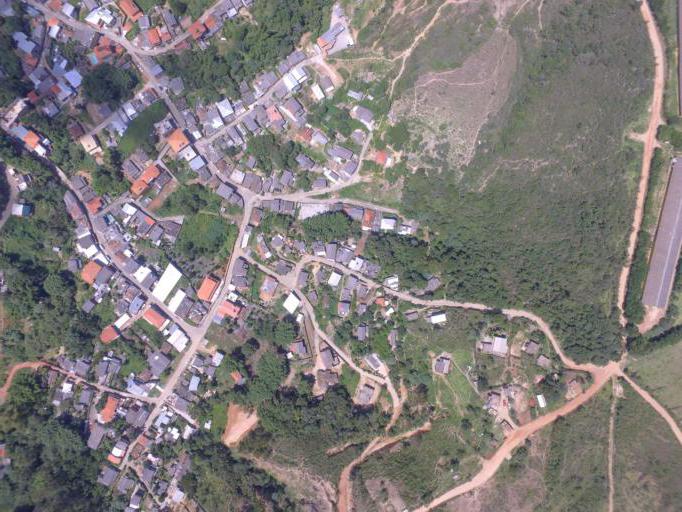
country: BR
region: Minas Gerais
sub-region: Tiradentes
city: Tiradentes
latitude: -21.0521
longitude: -44.0759
